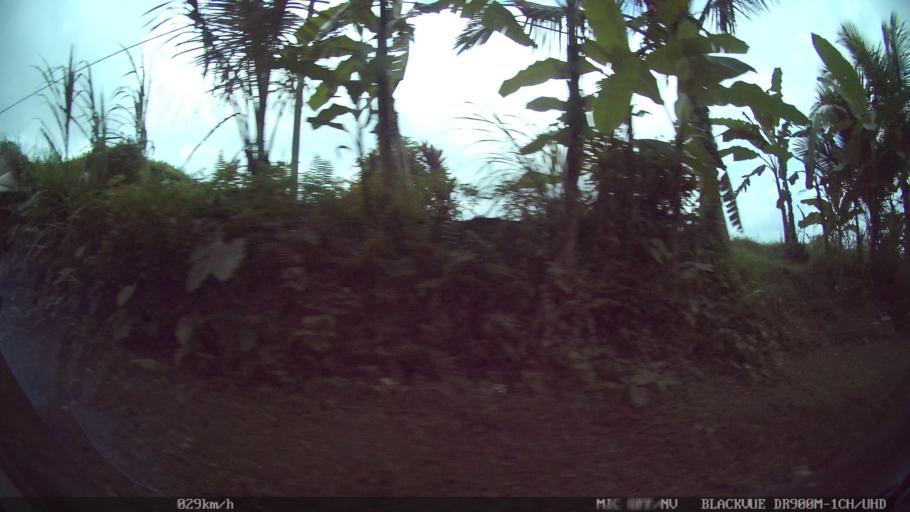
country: ID
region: Bali
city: Badung
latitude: -8.4240
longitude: 115.2269
